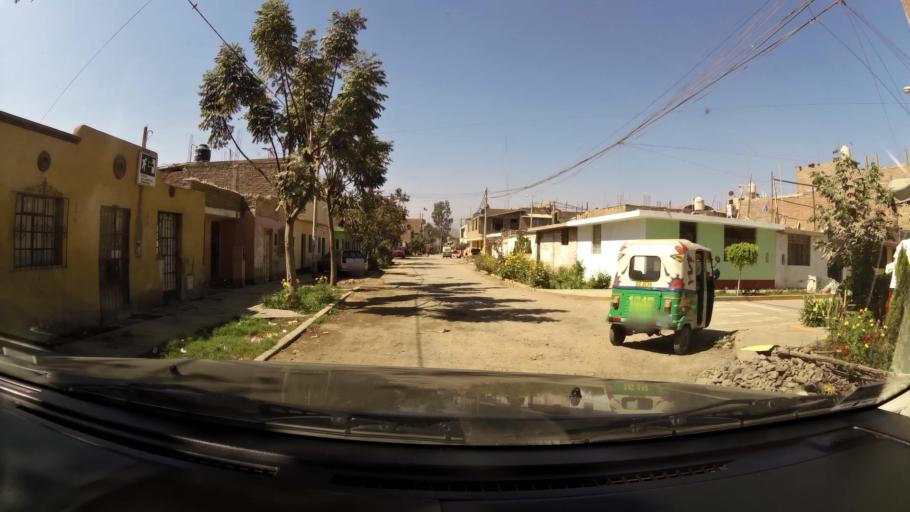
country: PE
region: Ica
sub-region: Provincia de Ica
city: Ica
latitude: -14.0564
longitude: -75.7253
